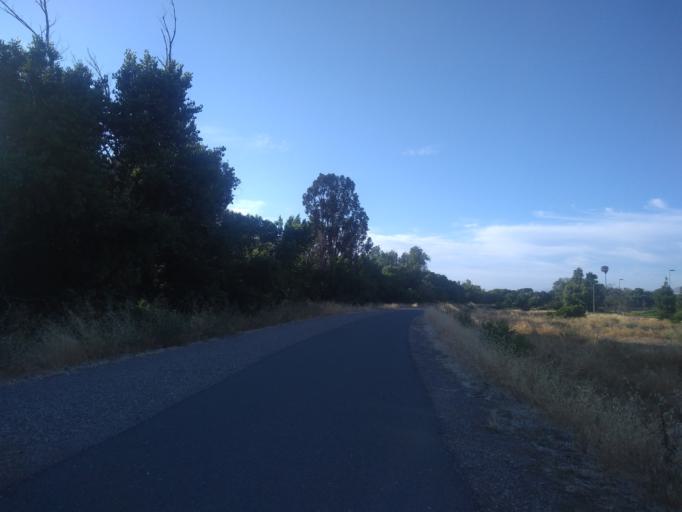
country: US
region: California
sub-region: Santa Clara County
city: Milpitas
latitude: 37.4286
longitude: -121.9280
